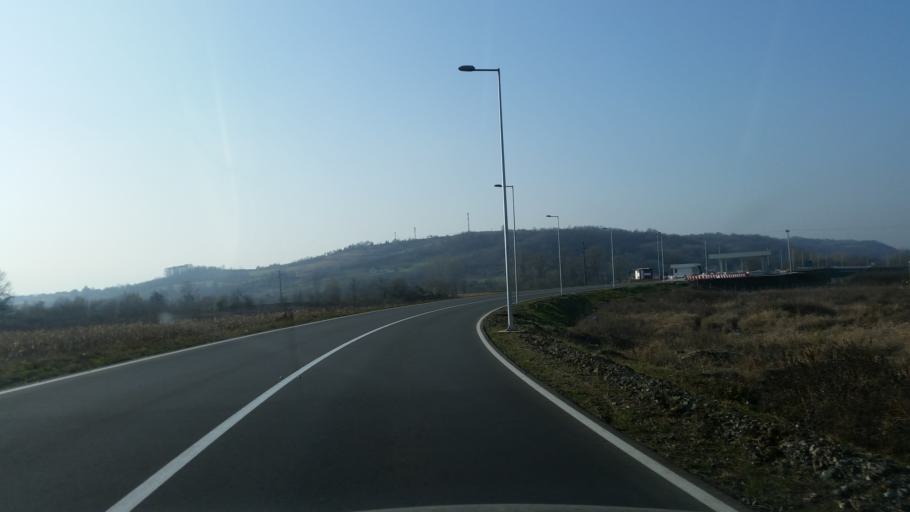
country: RS
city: Prislonica
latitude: 43.9175
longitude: 20.4037
